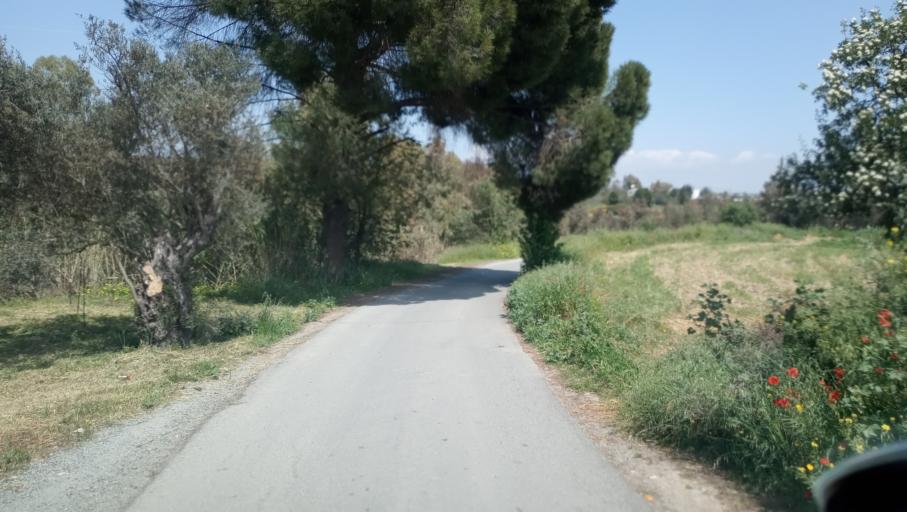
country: CY
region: Lefkosia
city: Dali
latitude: 35.0219
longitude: 33.4083
